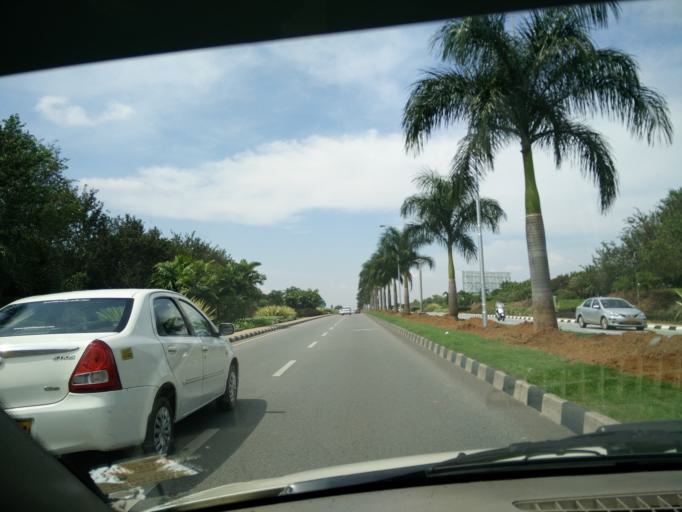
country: IN
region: Karnataka
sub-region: Bangalore Rural
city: Devanhalli
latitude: 13.1980
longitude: 77.6916
